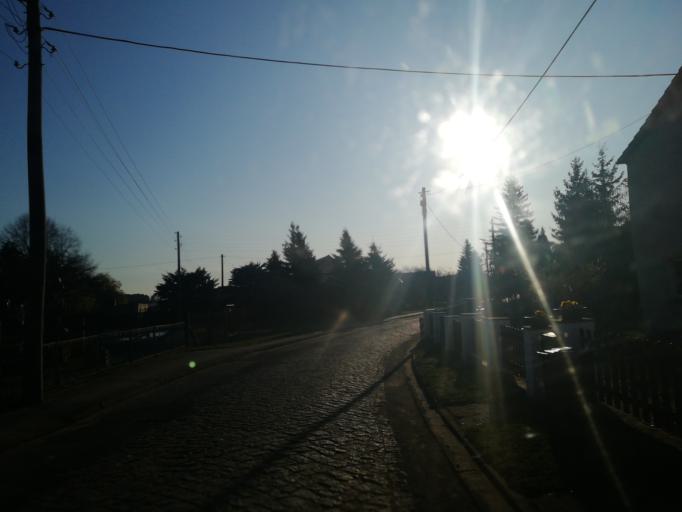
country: DE
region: Brandenburg
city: Drahnsdorf
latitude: 51.8937
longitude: 13.6031
